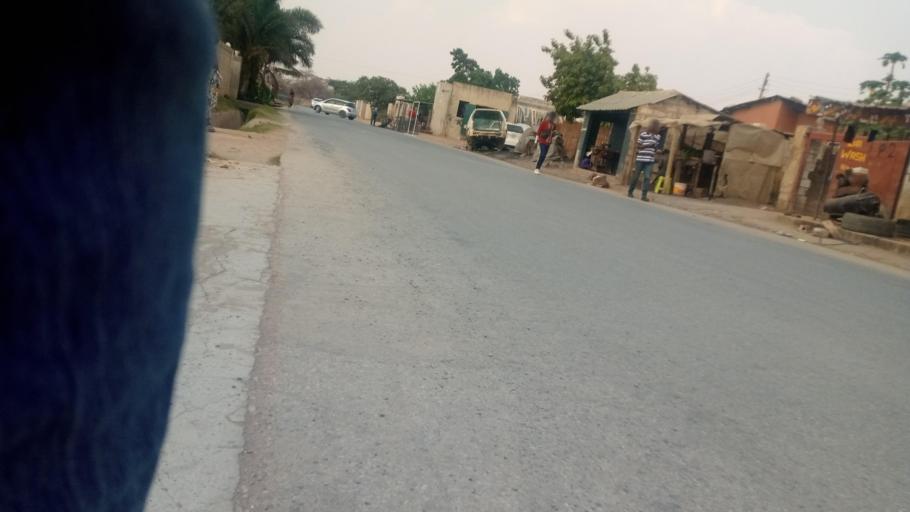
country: ZM
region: Lusaka
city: Lusaka
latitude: -15.4376
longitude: 28.3802
